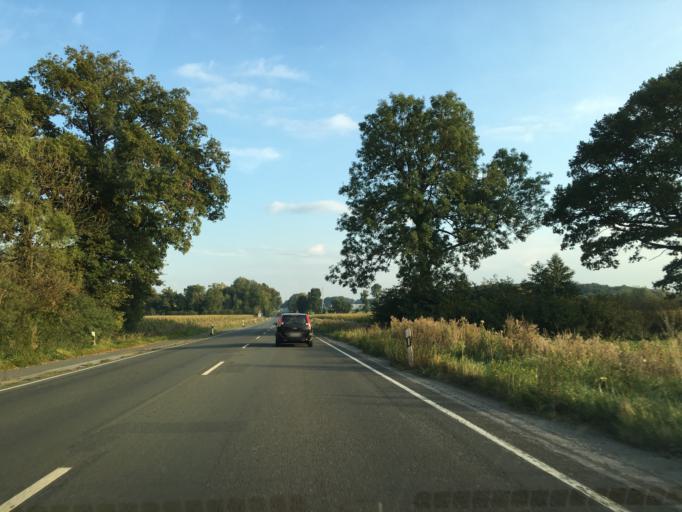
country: DE
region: North Rhine-Westphalia
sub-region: Regierungsbezirk Munster
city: Altenberge
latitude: 52.0297
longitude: 7.4865
